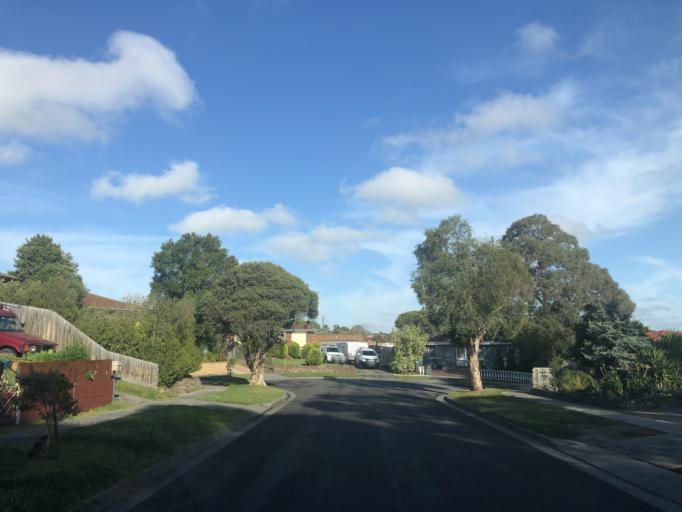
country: AU
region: Victoria
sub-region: Casey
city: Eumemmerring
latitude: -37.9983
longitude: 145.2635
